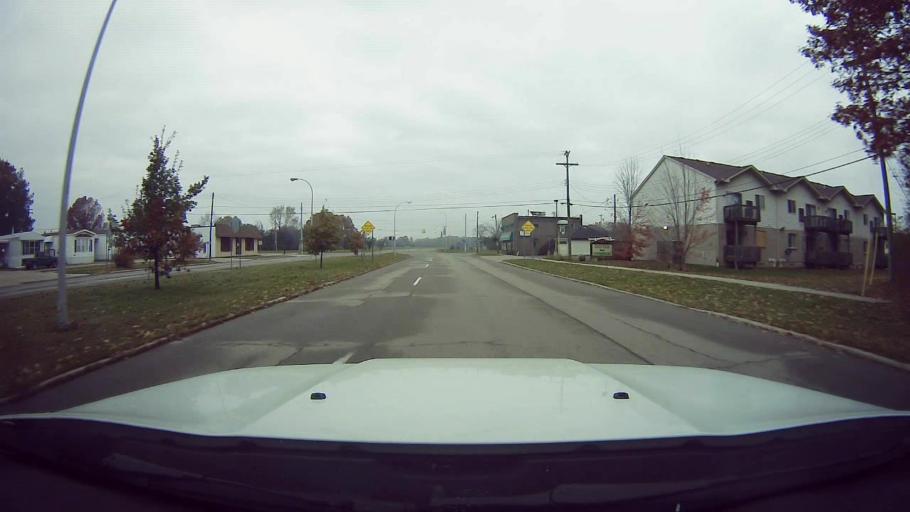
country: US
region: Michigan
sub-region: Wayne County
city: Dearborn Heights
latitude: 42.3411
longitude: -83.2517
